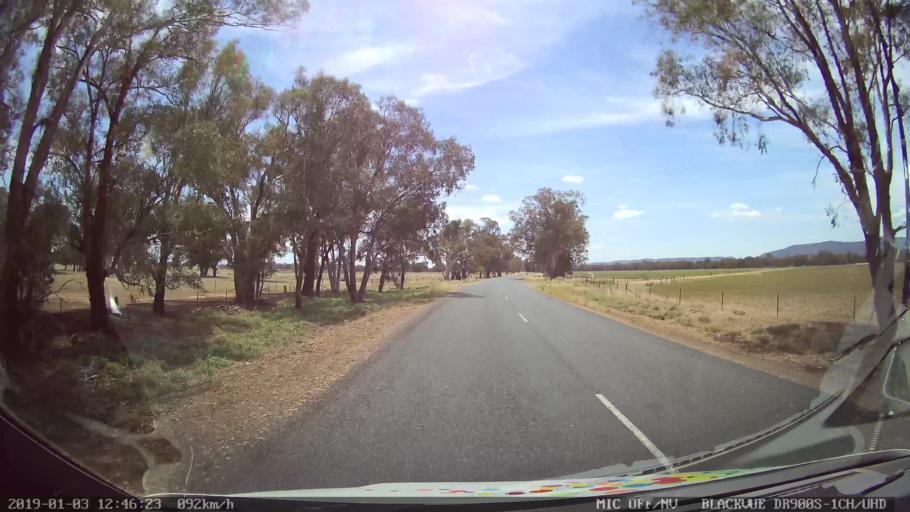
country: AU
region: New South Wales
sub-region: Weddin
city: Grenfell
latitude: -33.7387
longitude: 148.2327
